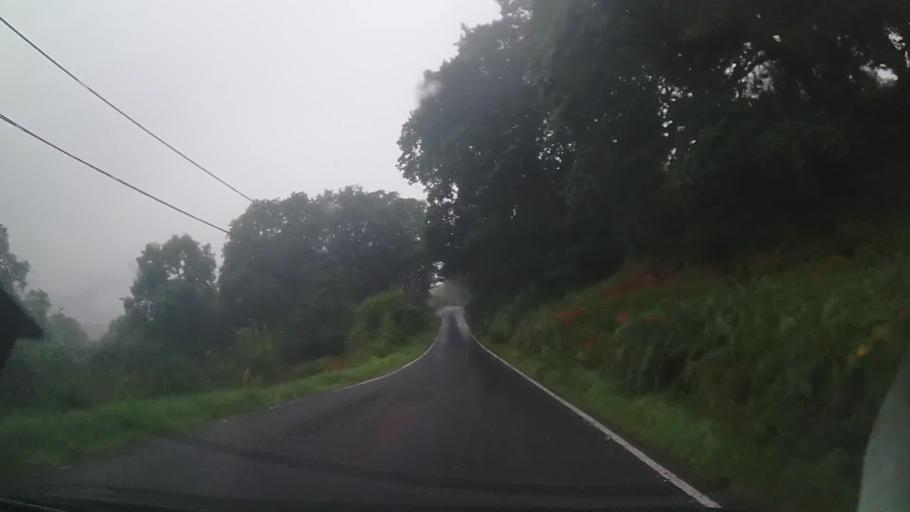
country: GB
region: Scotland
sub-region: Argyll and Bute
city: Isle Of Mull
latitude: 56.6878
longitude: -5.6226
